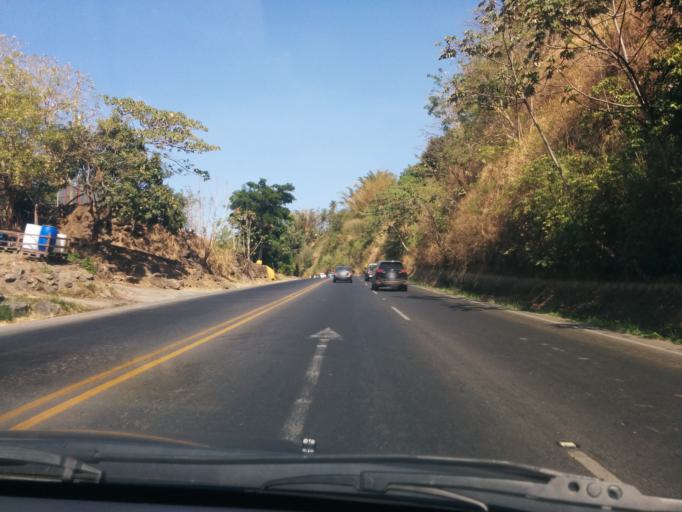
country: CR
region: Alajuela
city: Carrillos
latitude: 10.0029
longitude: -84.3039
